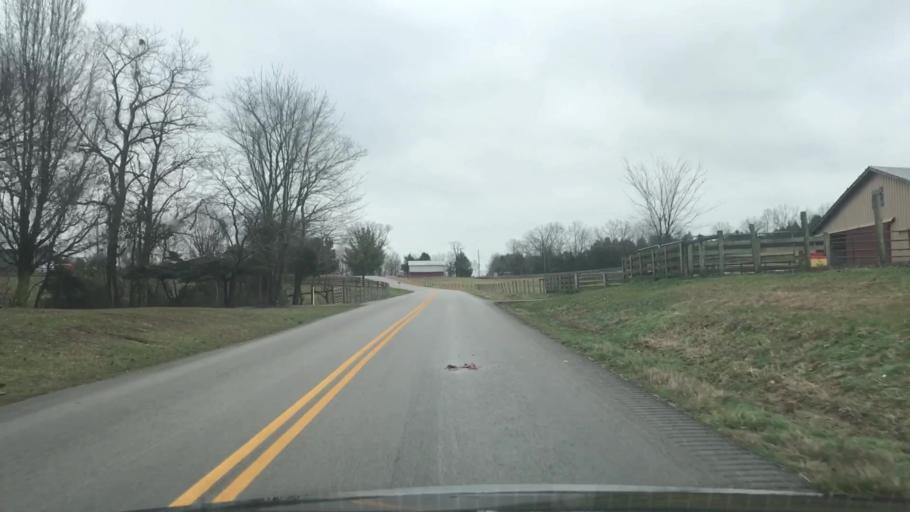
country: US
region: Kentucky
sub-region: Barren County
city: Glasgow
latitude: 36.9089
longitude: -85.7985
